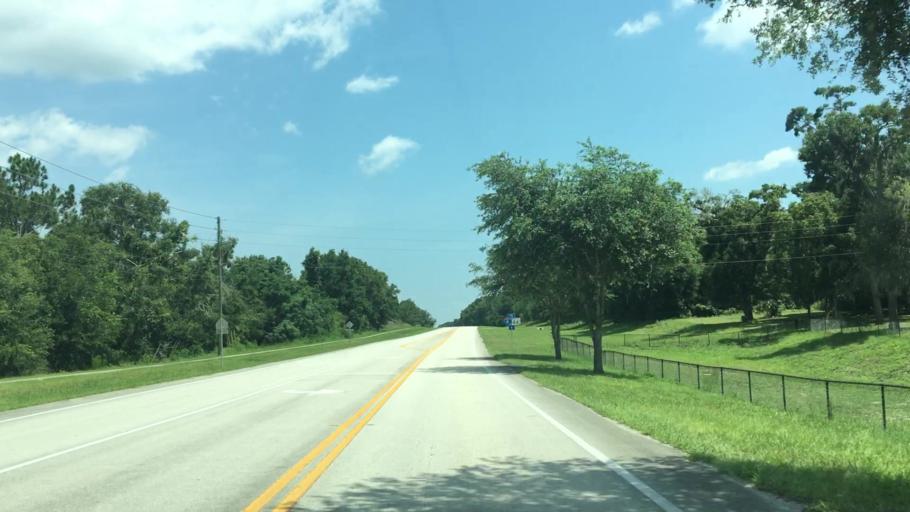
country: US
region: Florida
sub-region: Volusia County
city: Lake Helen
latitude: 28.9709
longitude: -81.2235
